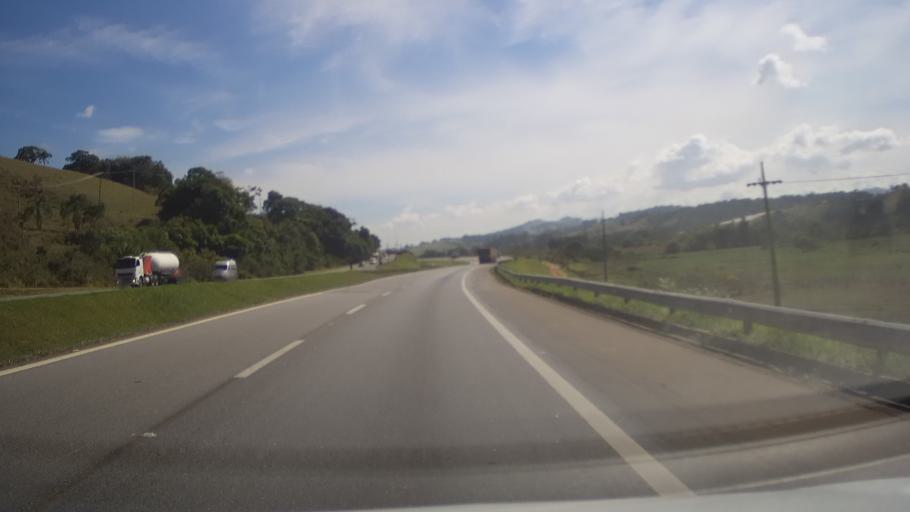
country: BR
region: Minas Gerais
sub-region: Cambui
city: Cambui
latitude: -22.5799
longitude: -46.0448
